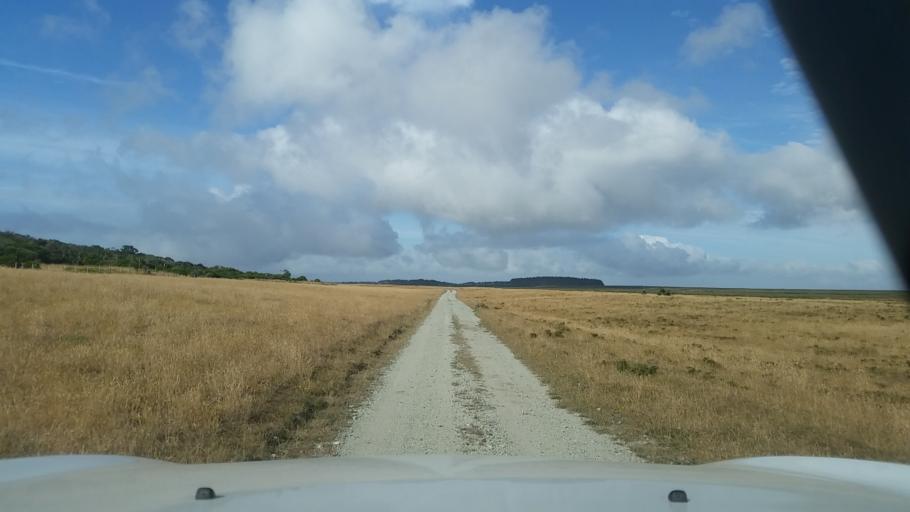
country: NZ
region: Chatham Islands
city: Waitangi
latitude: -43.7795
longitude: -176.3266
